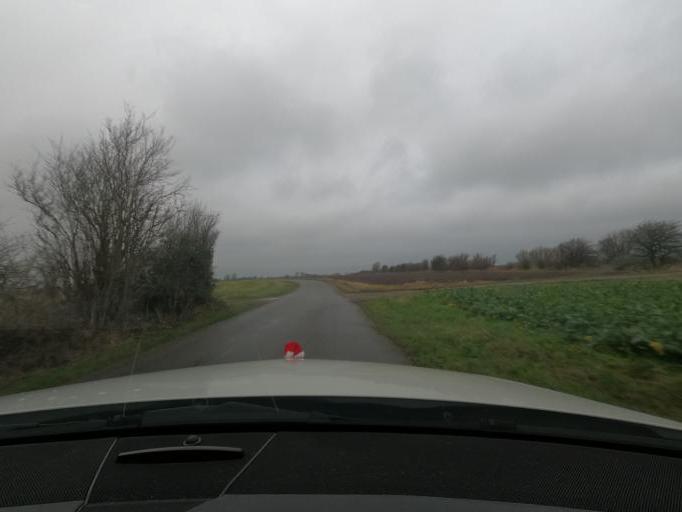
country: DK
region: South Denmark
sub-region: Haderslev Kommune
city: Starup
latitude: 55.1903
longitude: 9.6434
